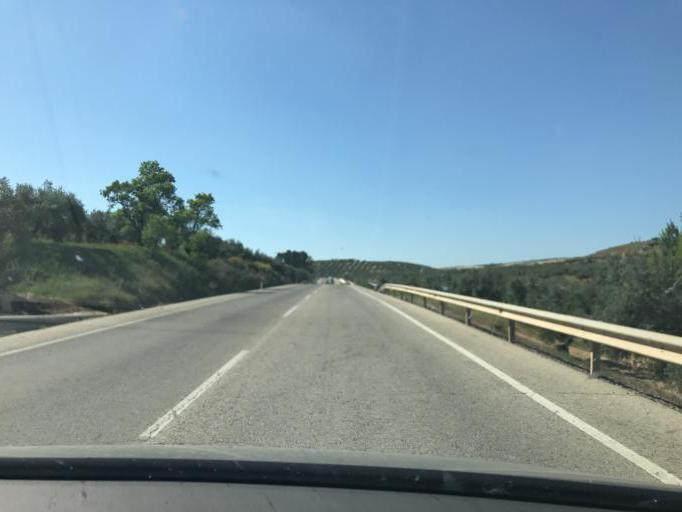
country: ES
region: Andalusia
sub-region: Province of Cordoba
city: Luque
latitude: 37.5682
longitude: -4.2487
